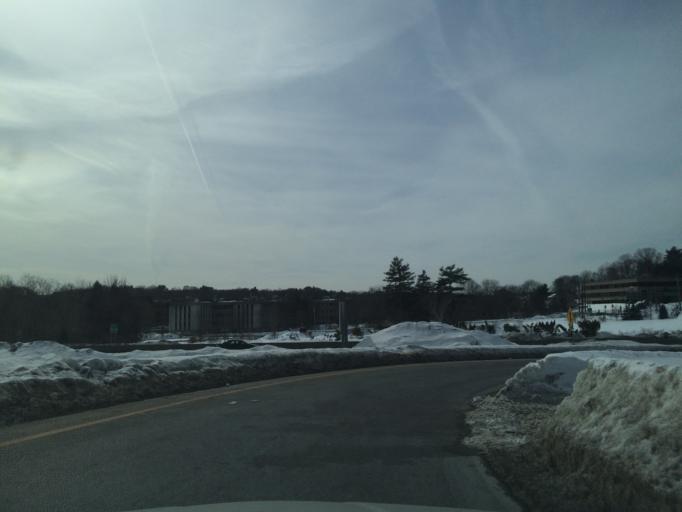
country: US
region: Massachusetts
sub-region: Middlesex County
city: Newton
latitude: 42.3278
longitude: -71.2503
